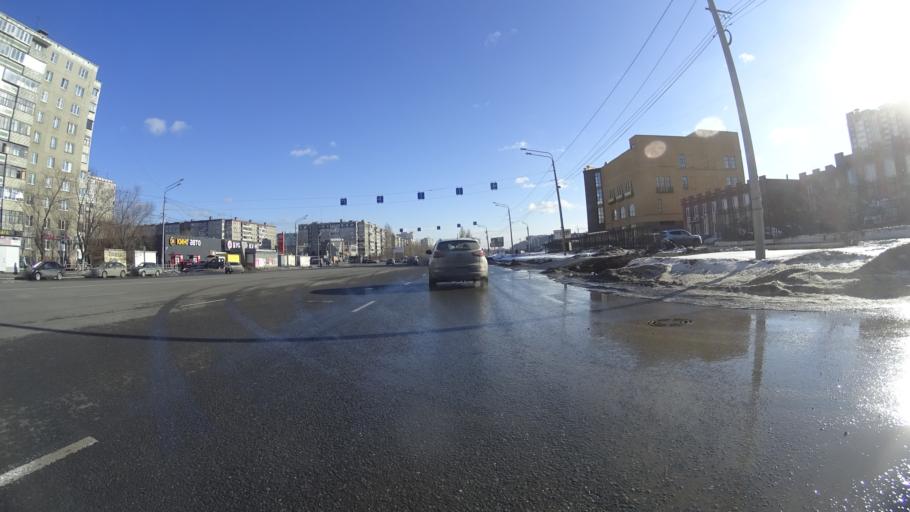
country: RU
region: Chelyabinsk
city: Roshchino
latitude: 55.1880
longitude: 61.2847
